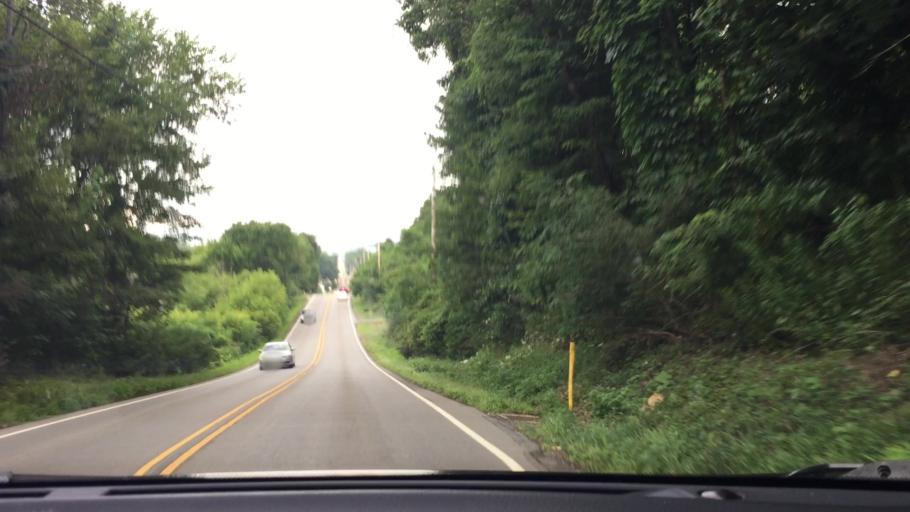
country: US
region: Pennsylvania
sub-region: Butler County
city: Fernway
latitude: 40.6813
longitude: -80.1434
